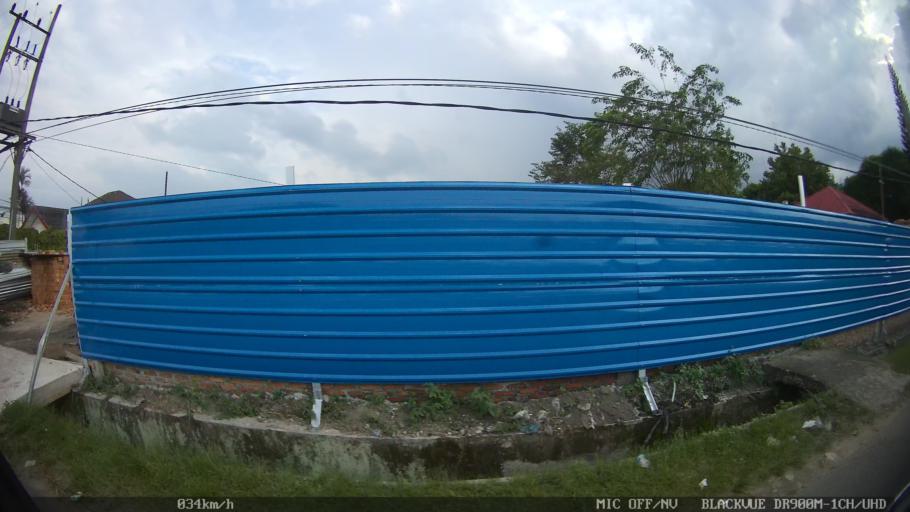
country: ID
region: North Sumatra
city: Sunggal
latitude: 3.5549
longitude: 98.6307
